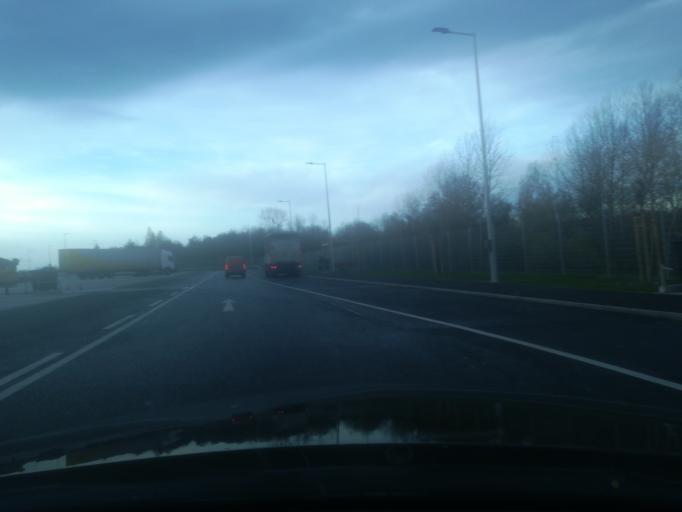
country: AT
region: Upper Austria
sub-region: Wels-Land
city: Marchtrenk
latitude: 48.1868
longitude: 14.1566
